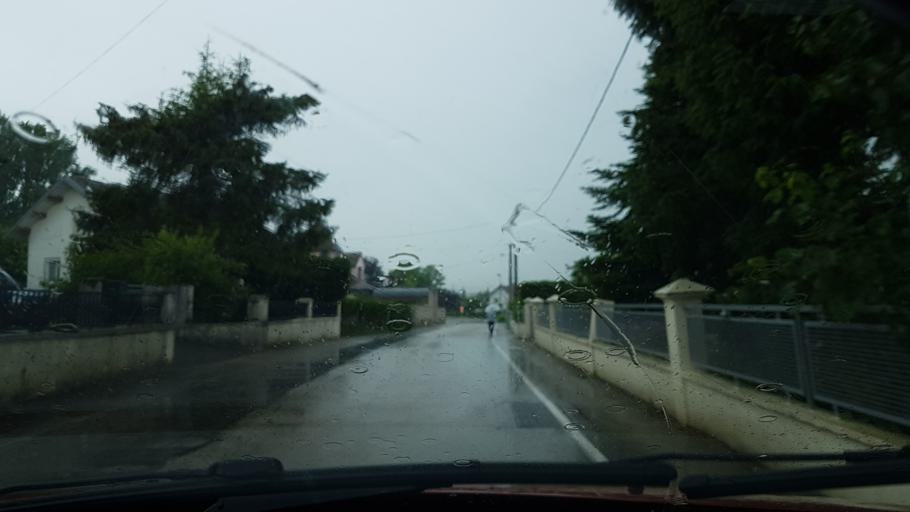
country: FR
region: Franche-Comte
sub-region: Departement du Jura
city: Clairvaux-les-Lacs
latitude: 46.5809
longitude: 5.6934
